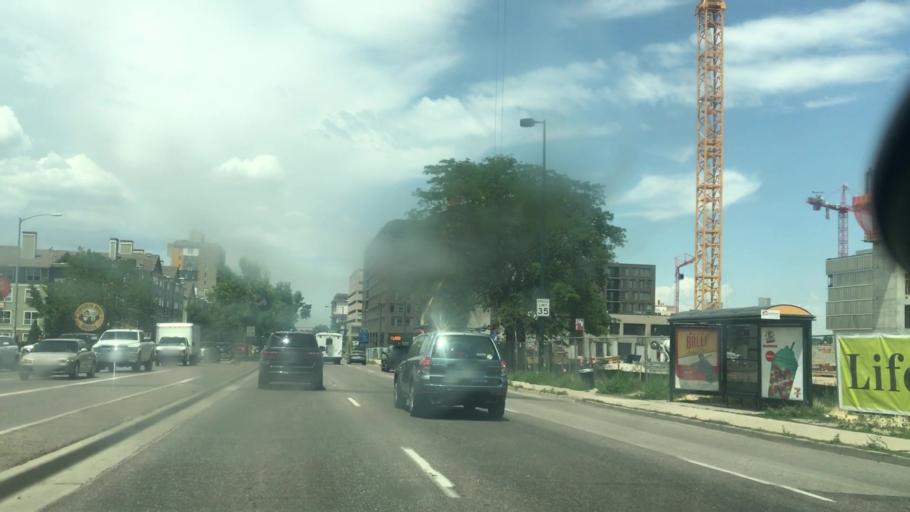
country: US
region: Colorado
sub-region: Arapahoe County
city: Glendale
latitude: 39.7295
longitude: -104.9407
